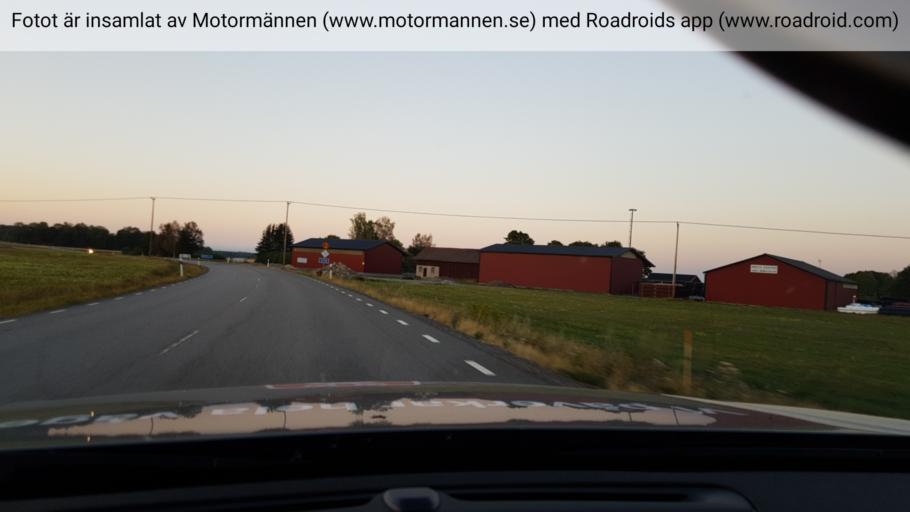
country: SE
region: Uppsala
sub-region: Heby Kommun
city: OEstervala
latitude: 60.1132
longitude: 17.2133
